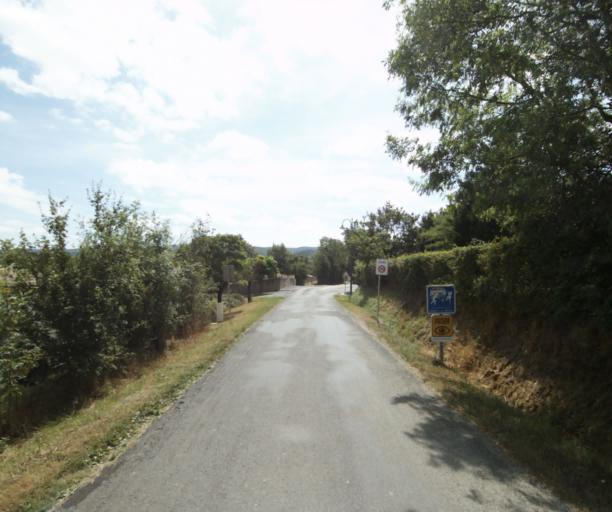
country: FR
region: Midi-Pyrenees
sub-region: Departement du Tarn
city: Soreze
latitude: 43.4718
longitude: 2.0774
